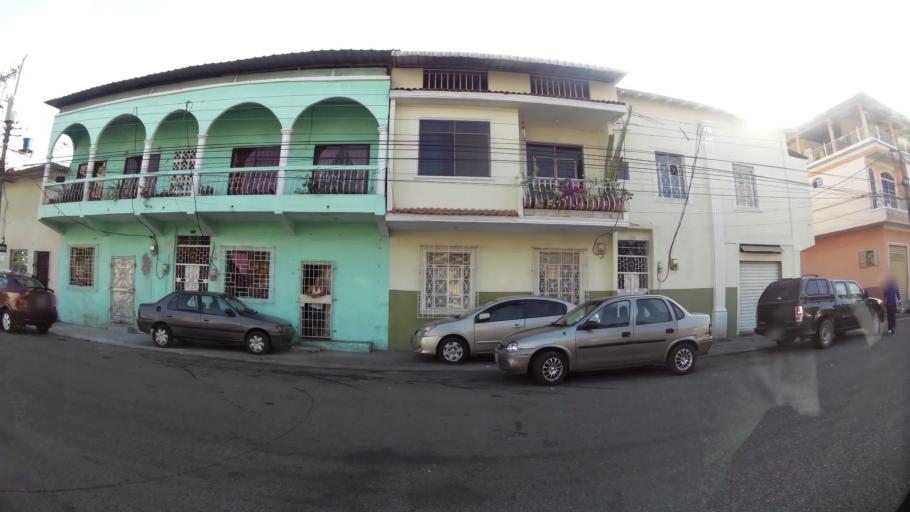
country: EC
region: Guayas
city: Eloy Alfaro
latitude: -2.1737
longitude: -79.8540
